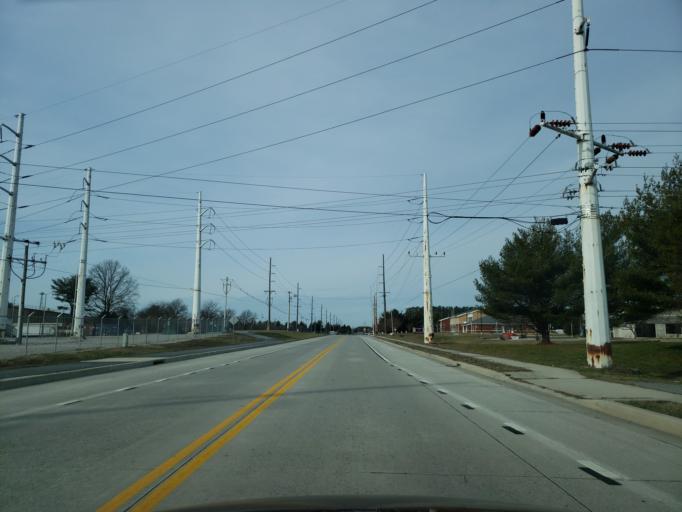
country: US
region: Delaware
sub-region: Kent County
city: Rodney Village
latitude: 39.1513
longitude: -75.5485
